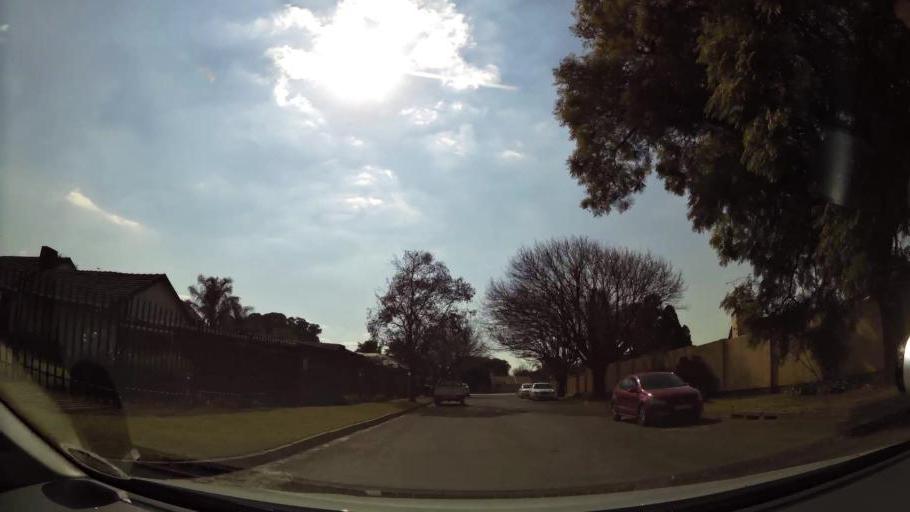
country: ZA
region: Gauteng
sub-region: City of Johannesburg Metropolitan Municipality
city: Modderfontein
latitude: -26.0855
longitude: 28.2274
